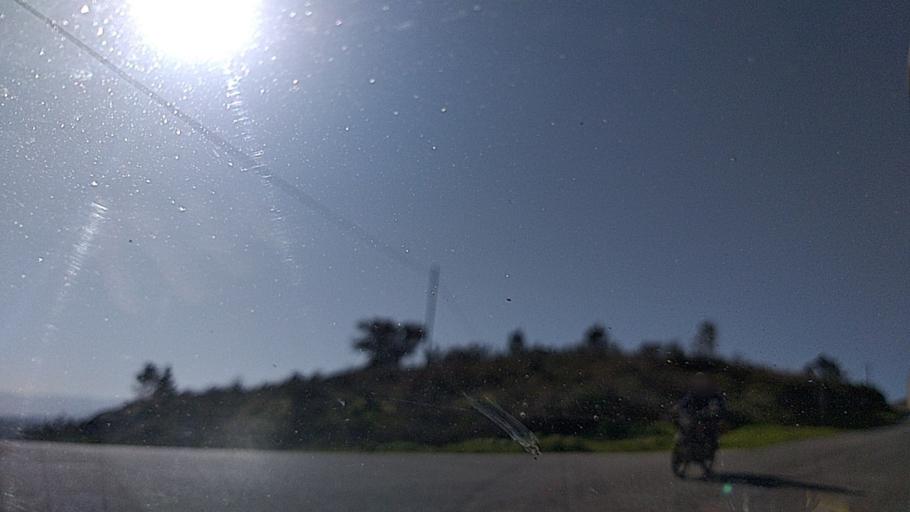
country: PT
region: Guarda
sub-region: Celorico da Beira
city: Celorico da Beira
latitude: 40.6795
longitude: -7.3968
